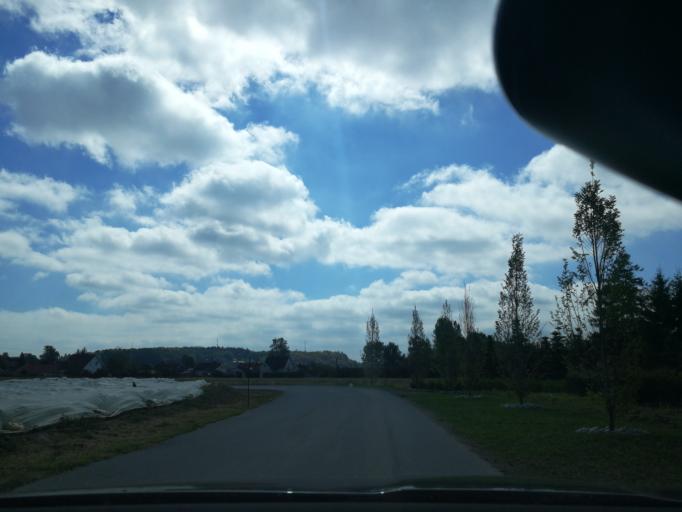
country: NO
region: Vestfold
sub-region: Sandefjord
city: Sandefjord
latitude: 59.1526
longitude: 10.1992
